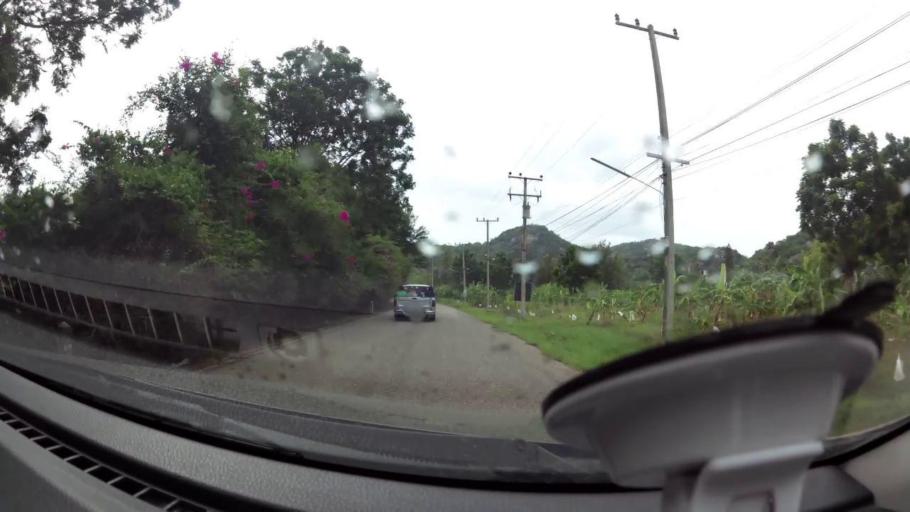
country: TH
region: Prachuap Khiri Khan
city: Pran Buri
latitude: 12.4331
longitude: 99.9775
